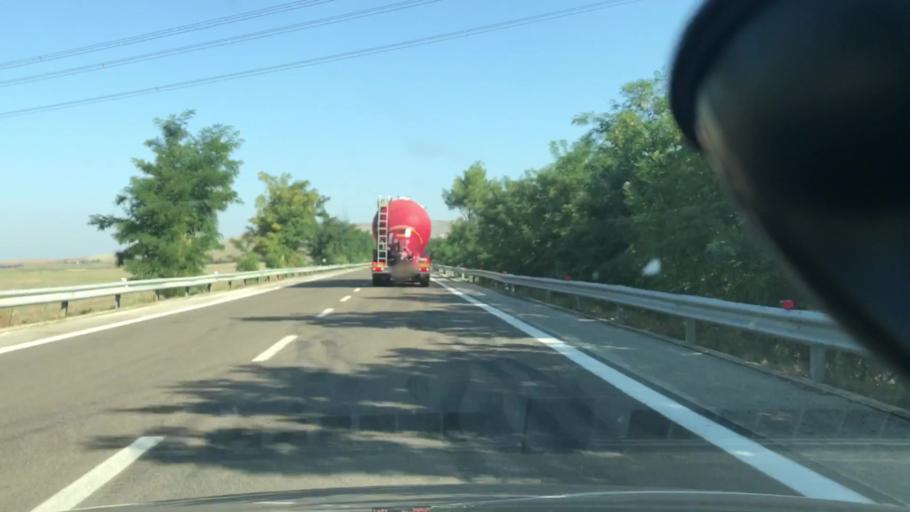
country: IT
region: Basilicate
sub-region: Provincia di Matera
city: Irsina
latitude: 40.7998
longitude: 16.2746
